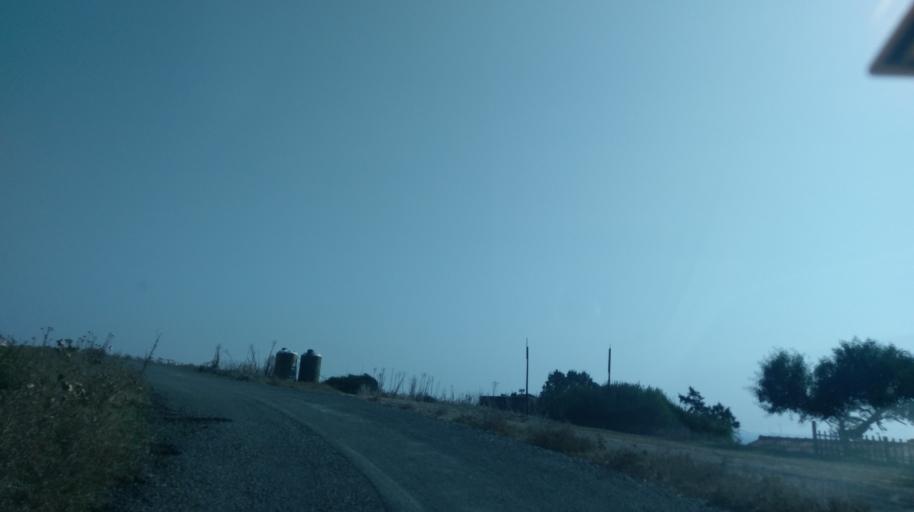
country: CY
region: Ammochostos
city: Rizokarpaso
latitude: 35.6452
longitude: 34.5540
